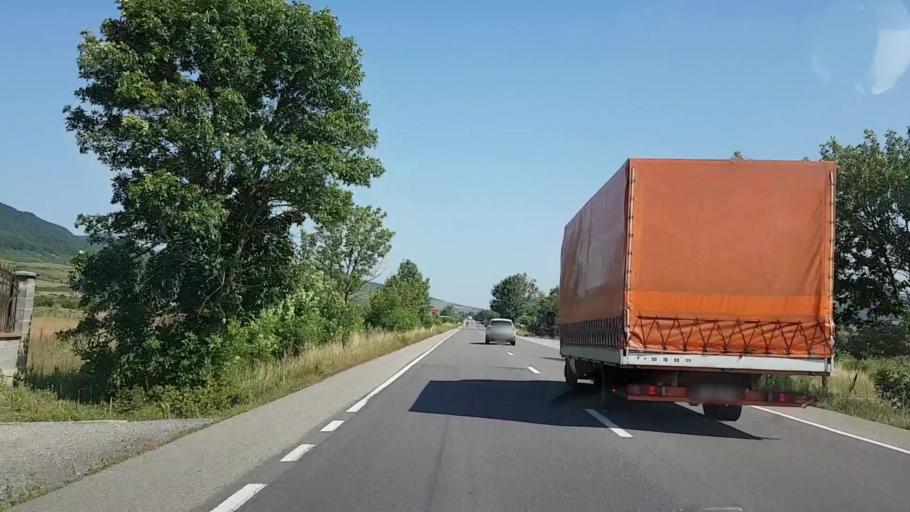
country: RO
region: Bistrita-Nasaud
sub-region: Comuna Sieu-Magherus
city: Sieu-Magherus
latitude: 47.1044
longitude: 24.3546
